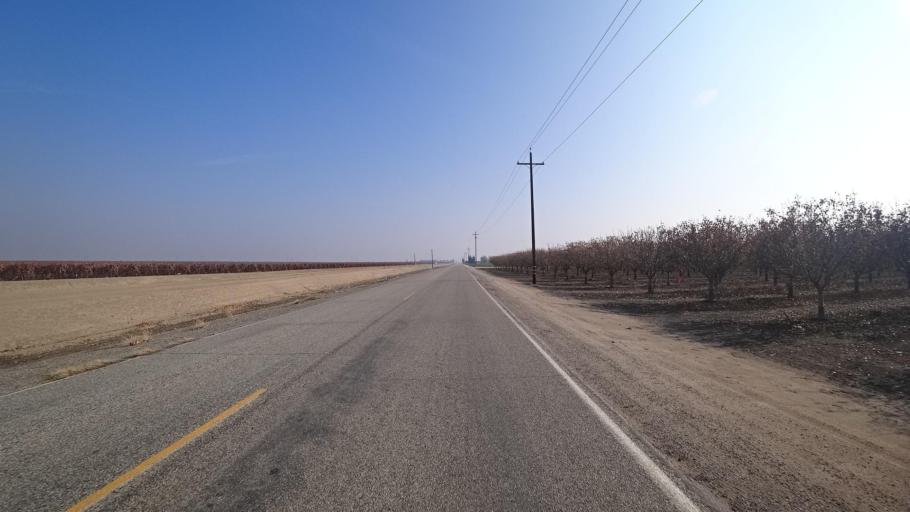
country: US
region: California
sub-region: Kern County
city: Buttonwillow
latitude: 35.3547
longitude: -119.3916
